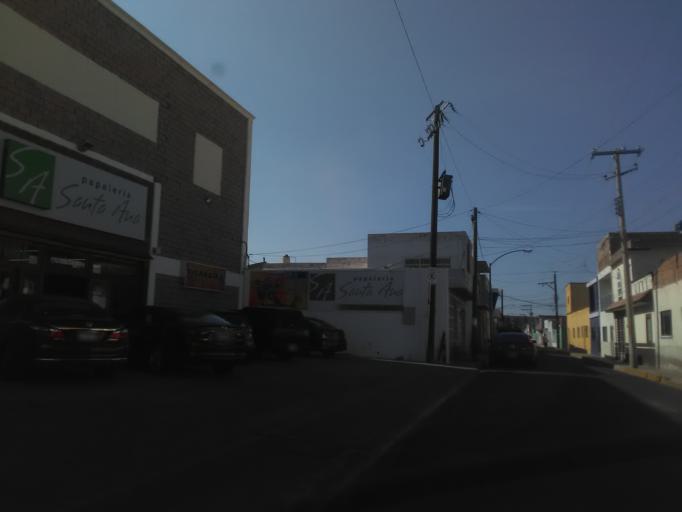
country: MX
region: Durango
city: Victoria de Durango
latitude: 24.0315
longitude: -104.6631
